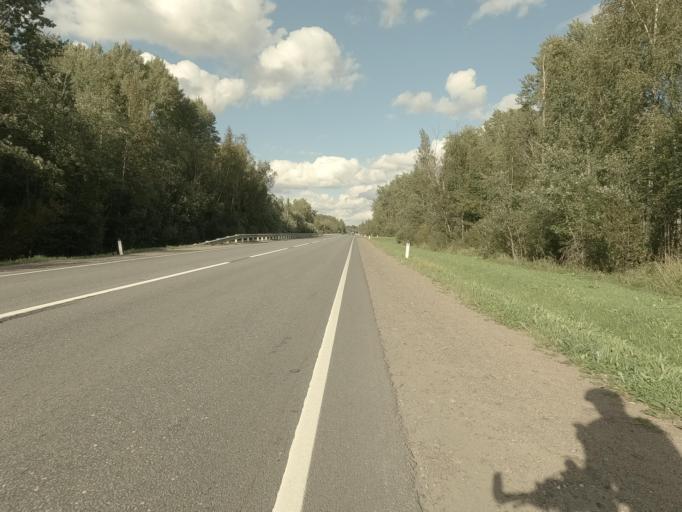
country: RU
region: Leningrad
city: Nikol'skoye
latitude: 59.6579
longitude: 30.8665
